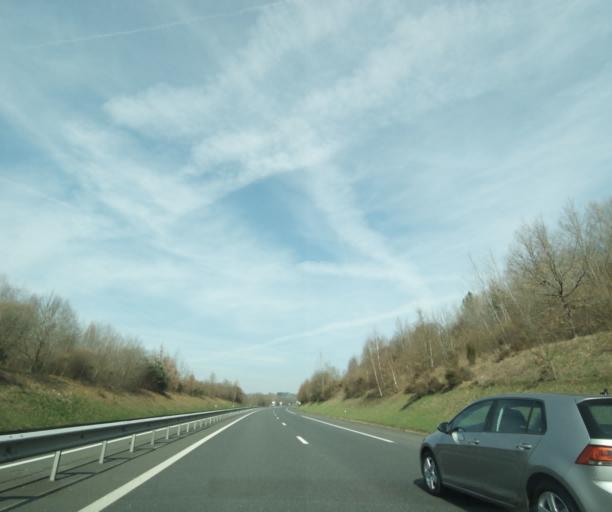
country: FR
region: Limousin
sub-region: Departement de la Correze
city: Vigeois
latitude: 45.4169
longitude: 1.5202
